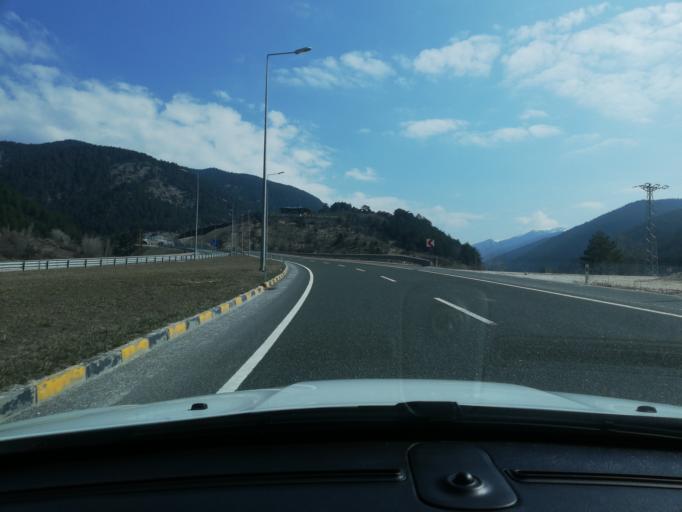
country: TR
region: Cankiri
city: Ilgaz
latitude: 41.0321
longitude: 33.7429
